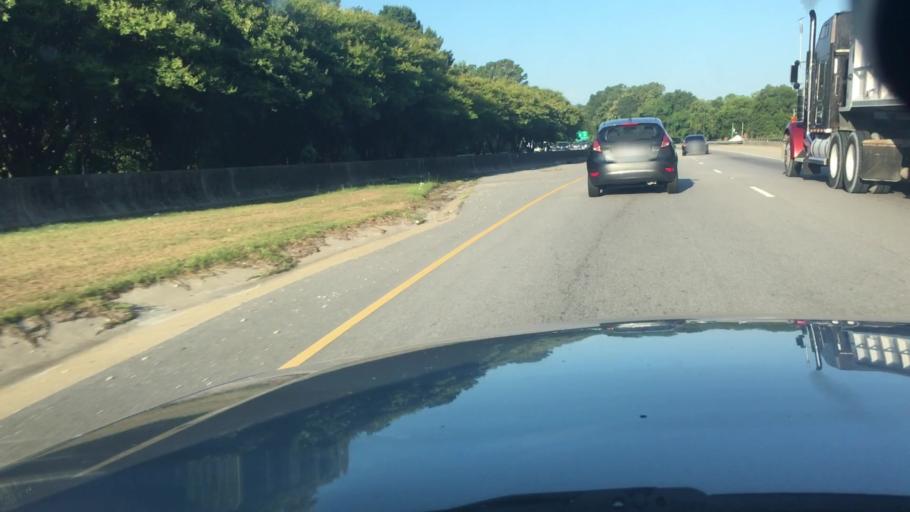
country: US
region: North Carolina
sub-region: Cumberland County
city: Fayetteville
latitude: 35.0701
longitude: -78.8814
